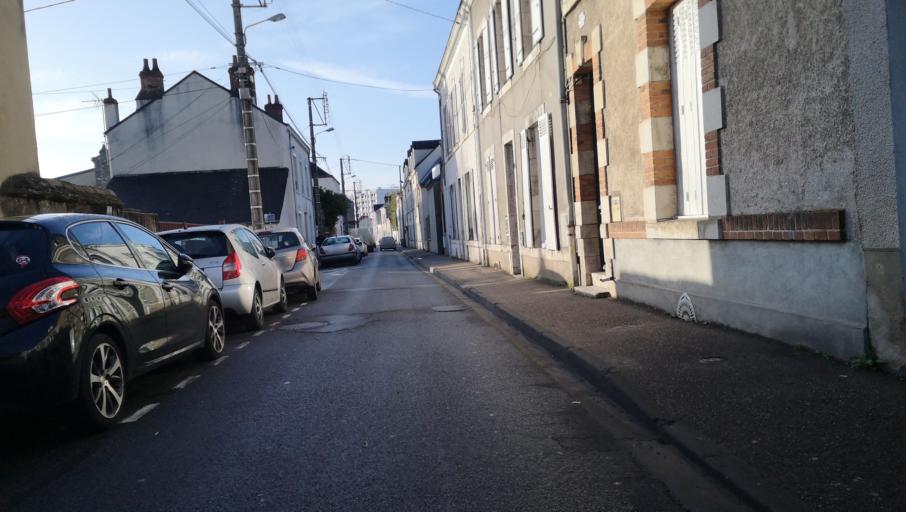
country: FR
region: Centre
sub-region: Departement du Loiret
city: Orleans
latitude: 47.9047
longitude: 1.8889
